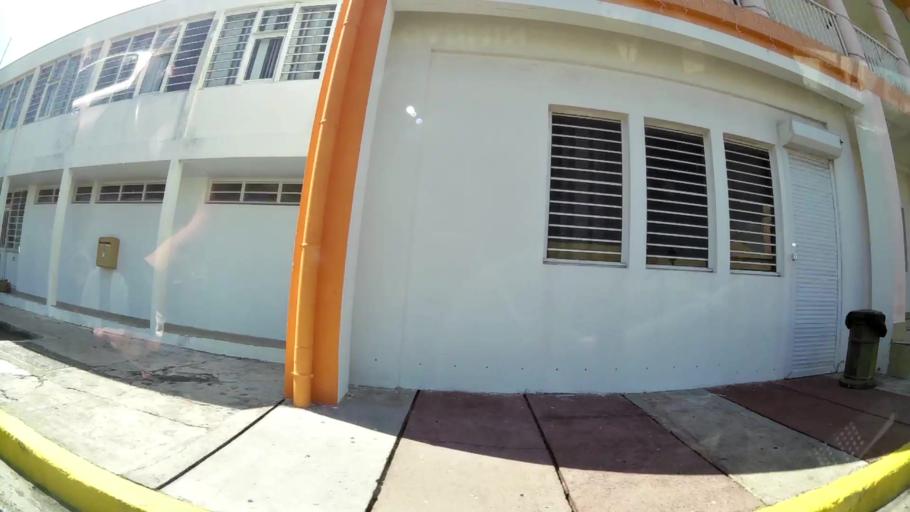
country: GP
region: Guadeloupe
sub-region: Guadeloupe
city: Saint-Francois
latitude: 16.2513
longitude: -61.2740
